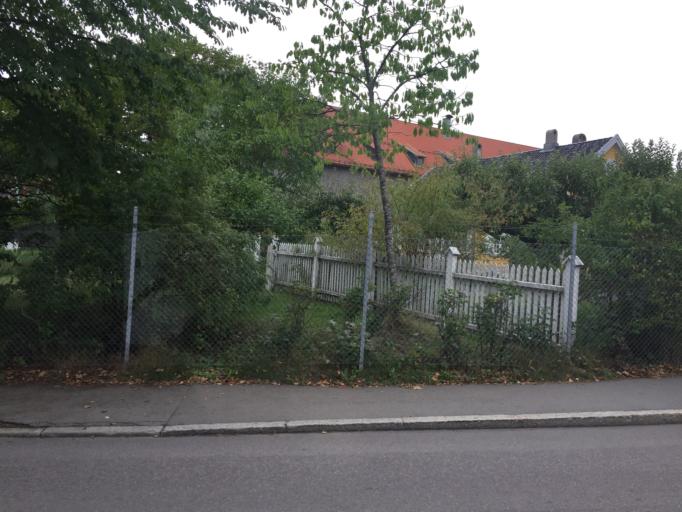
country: NO
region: Oslo
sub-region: Oslo
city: Sjolyststranda
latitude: 59.9068
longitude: 10.6879
